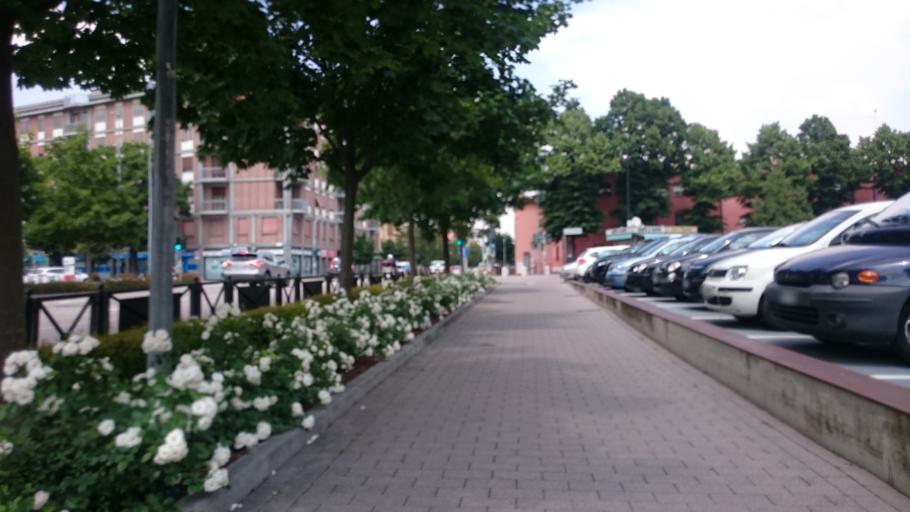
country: IT
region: Lombardy
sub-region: Provincia di Mantova
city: Mantova
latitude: 45.1473
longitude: 10.7958
